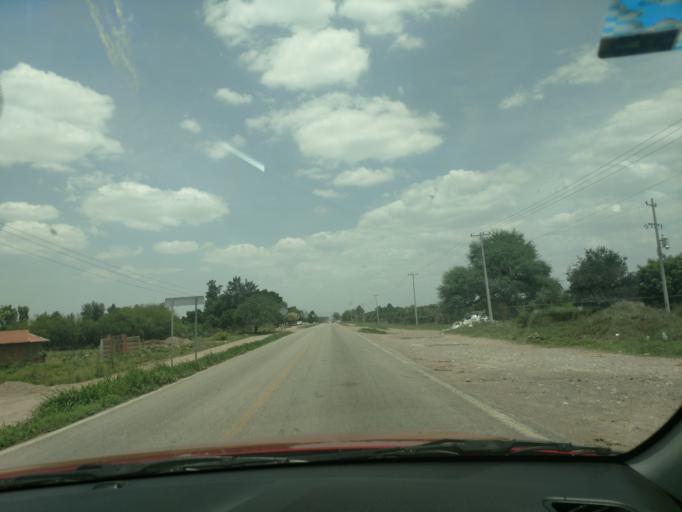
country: MX
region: San Luis Potosi
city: Ciudad Fernandez
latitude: 21.9501
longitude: -100.0625
